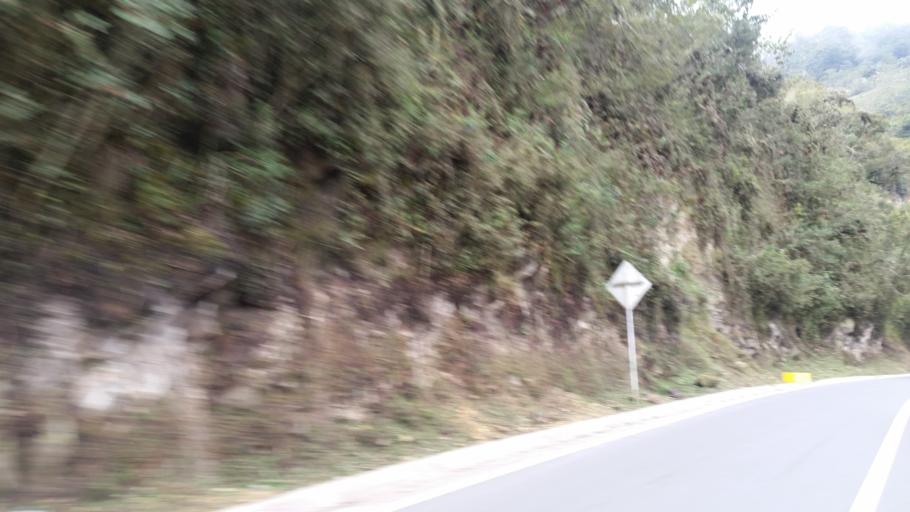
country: CO
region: Cundinamarca
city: Choachi
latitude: 4.5581
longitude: -73.9555
